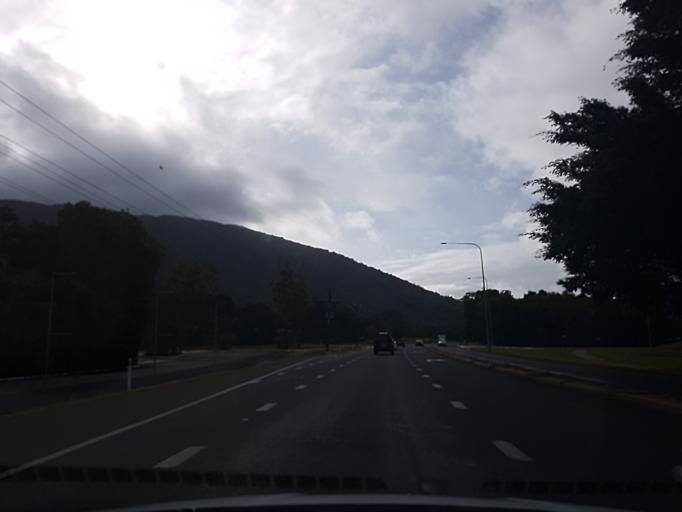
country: AU
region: Queensland
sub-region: Cairns
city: Palm Cove
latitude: -16.7579
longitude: 145.6631
